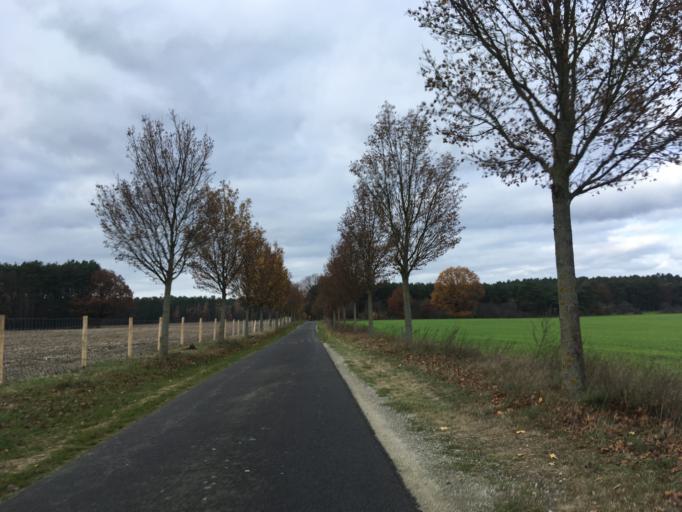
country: DE
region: Brandenburg
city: Tauer
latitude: 51.9860
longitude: 14.5234
